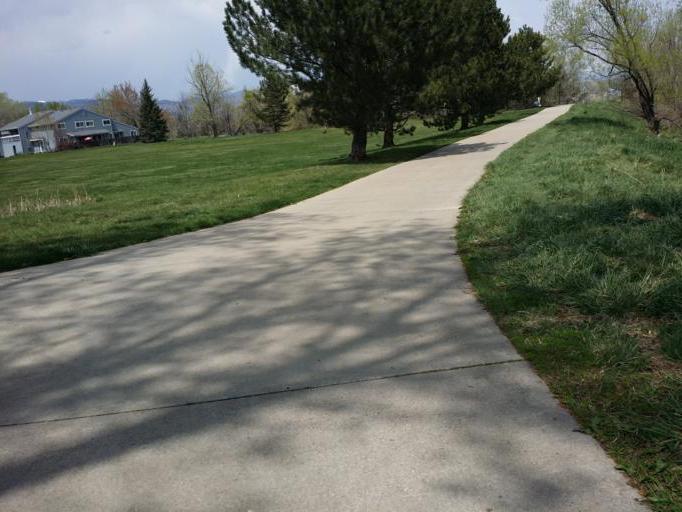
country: US
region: Colorado
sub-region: Boulder County
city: Boulder
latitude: 40.0062
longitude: -105.2398
